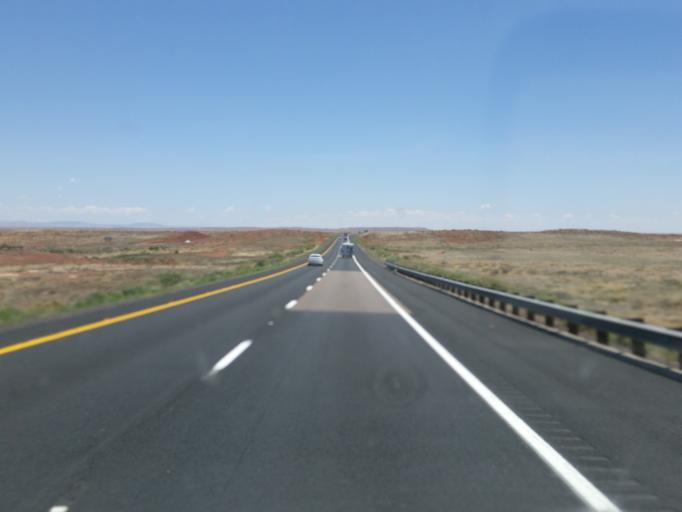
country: US
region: Arizona
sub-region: Coconino County
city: LeChee
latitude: 35.0988
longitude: -110.9685
